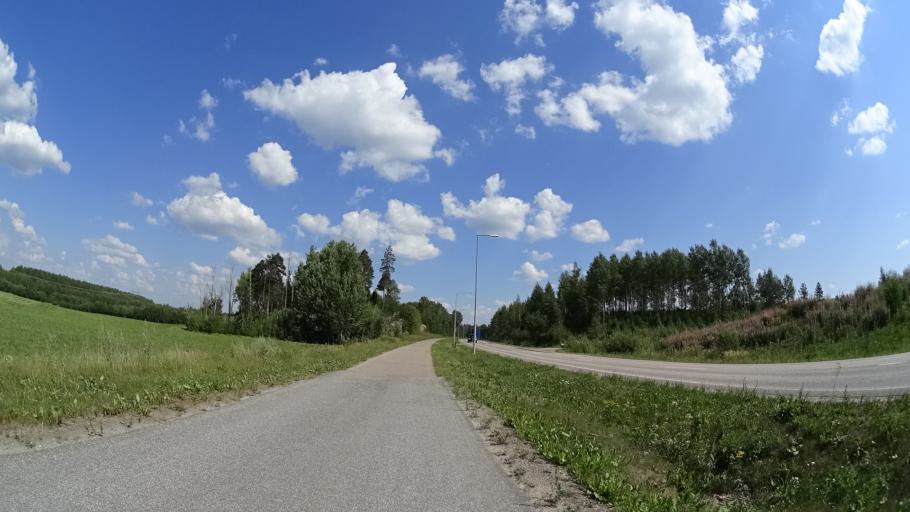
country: FI
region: Uusimaa
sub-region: Helsinki
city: Teekkarikylae
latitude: 60.3129
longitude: 24.8937
